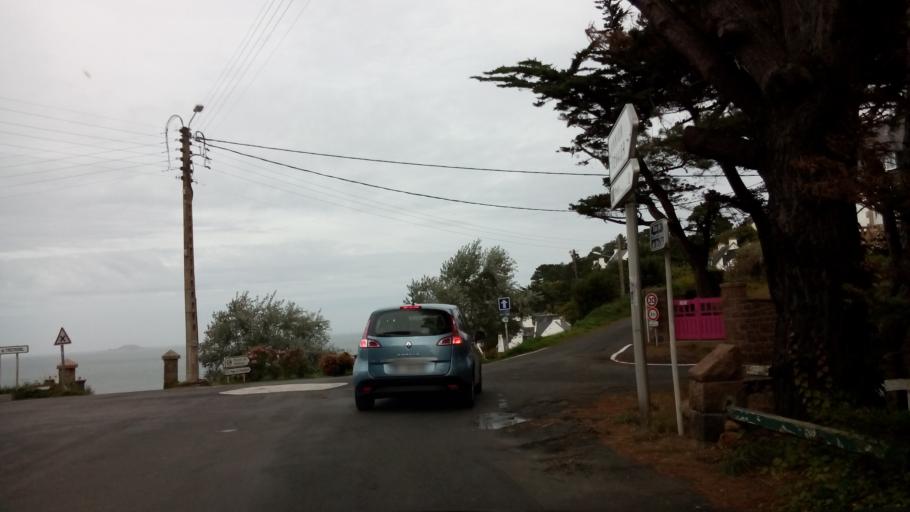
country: FR
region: Brittany
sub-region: Departement des Cotes-d'Armor
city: Perros-Guirec
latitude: 48.8169
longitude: -3.4307
